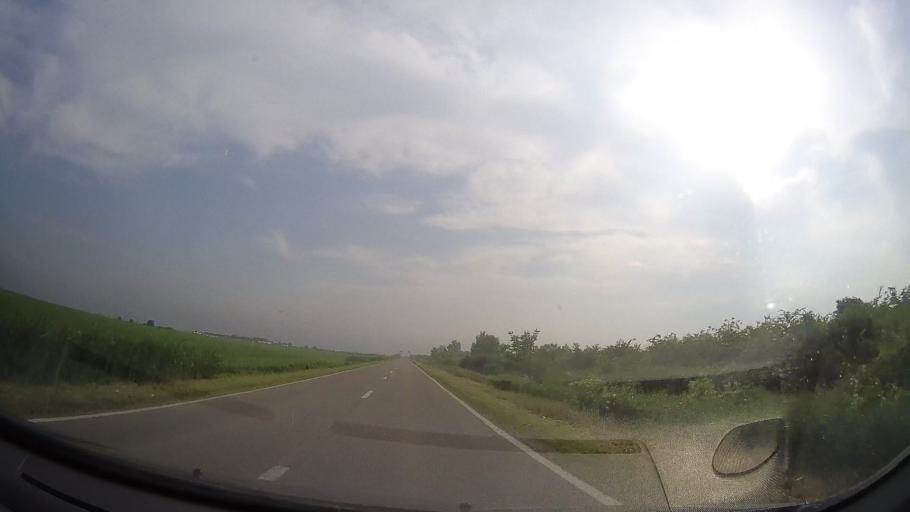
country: RO
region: Timis
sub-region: Comuna Peciu Nou
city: Peciu Nou
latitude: 45.6274
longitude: 21.0941
